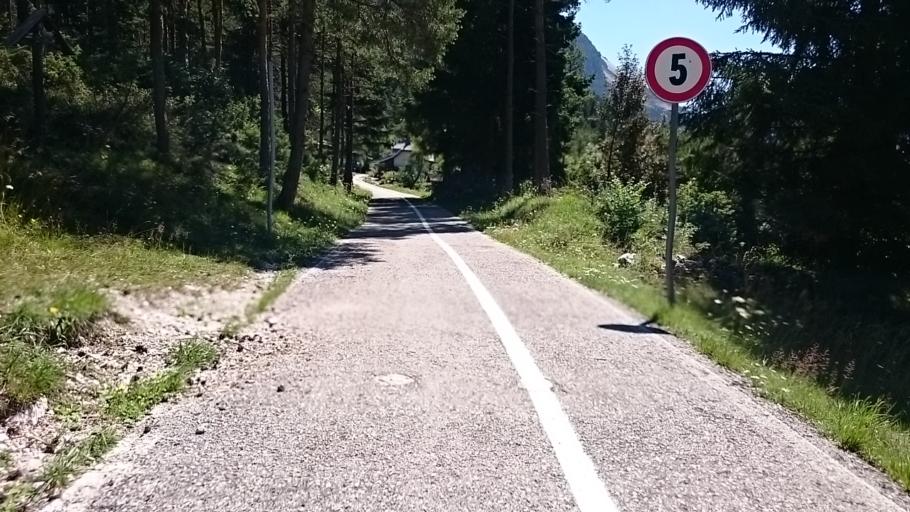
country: IT
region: Veneto
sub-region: Provincia di Belluno
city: San Vito
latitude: 46.4752
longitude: 12.2024
